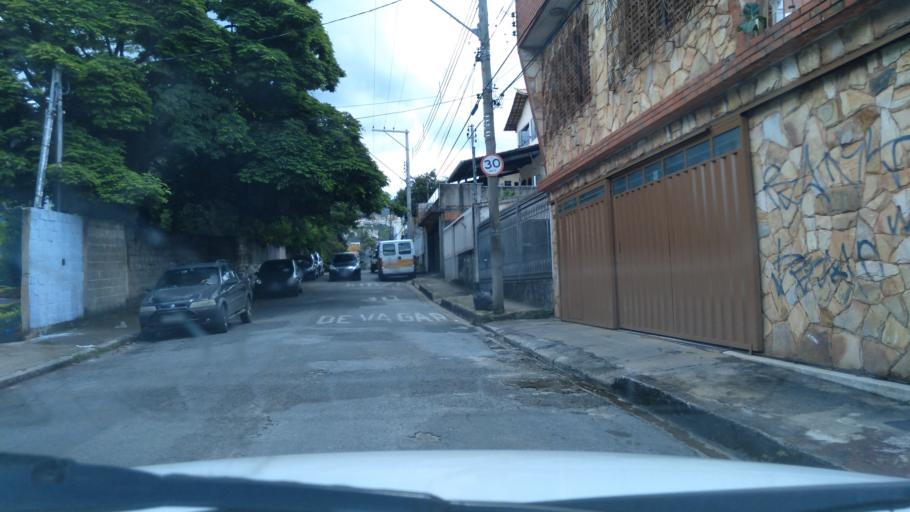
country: BR
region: Minas Gerais
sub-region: Belo Horizonte
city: Belo Horizonte
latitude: -19.9108
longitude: -43.8960
